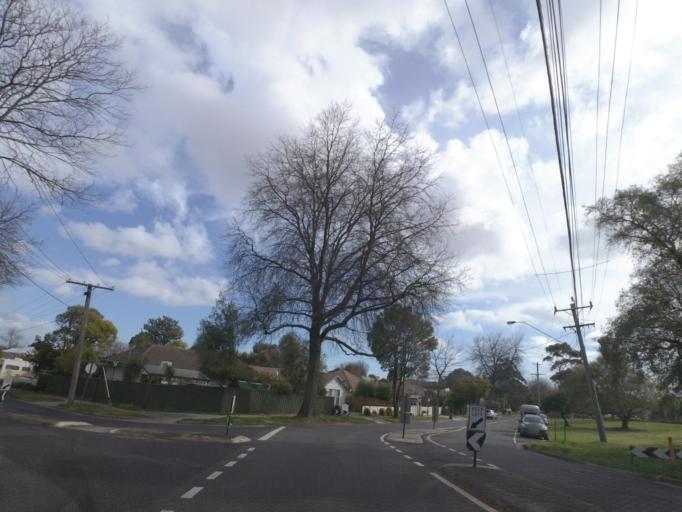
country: AU
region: Victoria
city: Forest Hill
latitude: -37.8245
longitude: 145.1889
